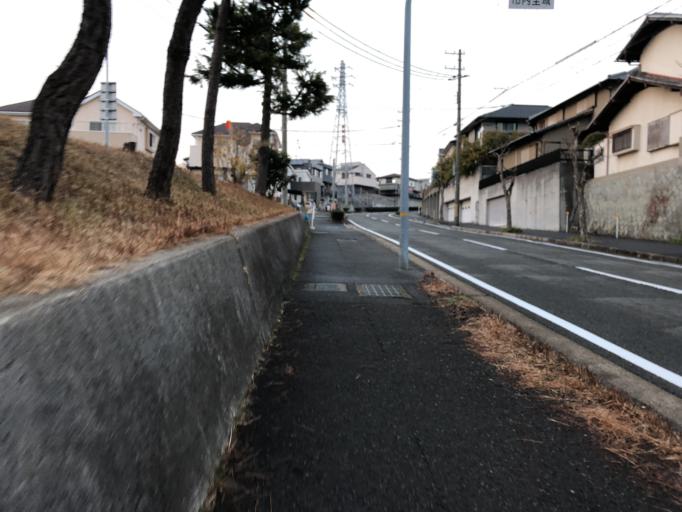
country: JP
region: Hyogo
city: Akashi
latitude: 34.6485
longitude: 135.0188
